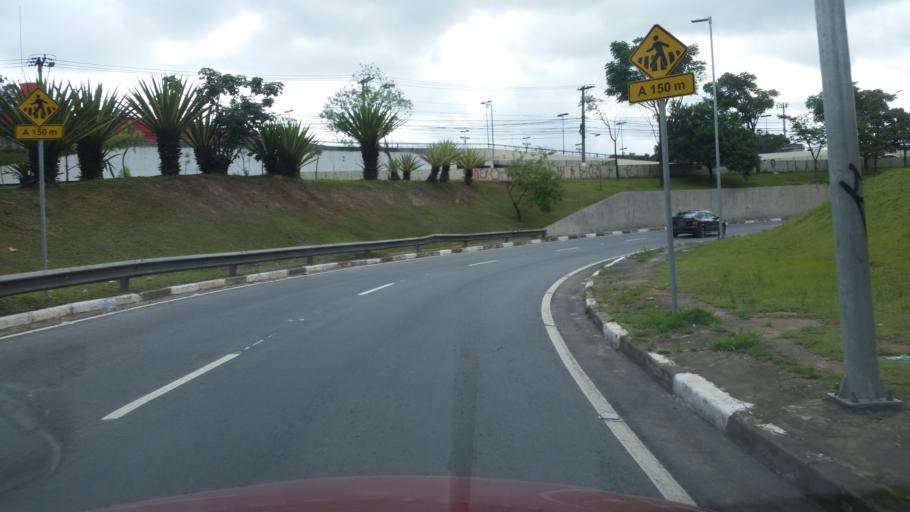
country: BR
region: Sao Paulo
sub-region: Taboao Da Serra
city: Taboao da Serra
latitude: -23.6456
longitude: -46.7279
